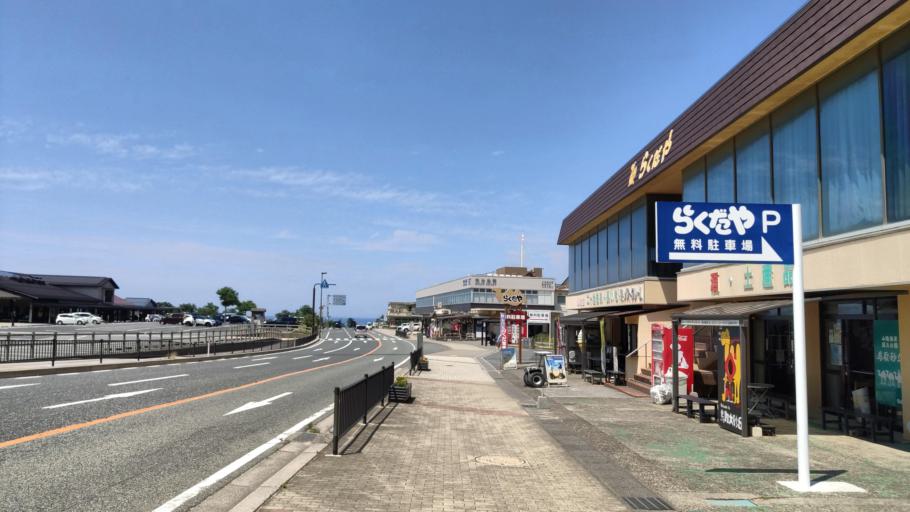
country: JP
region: Tottori
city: Tottori
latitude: 35.5428
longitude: 134.2368
